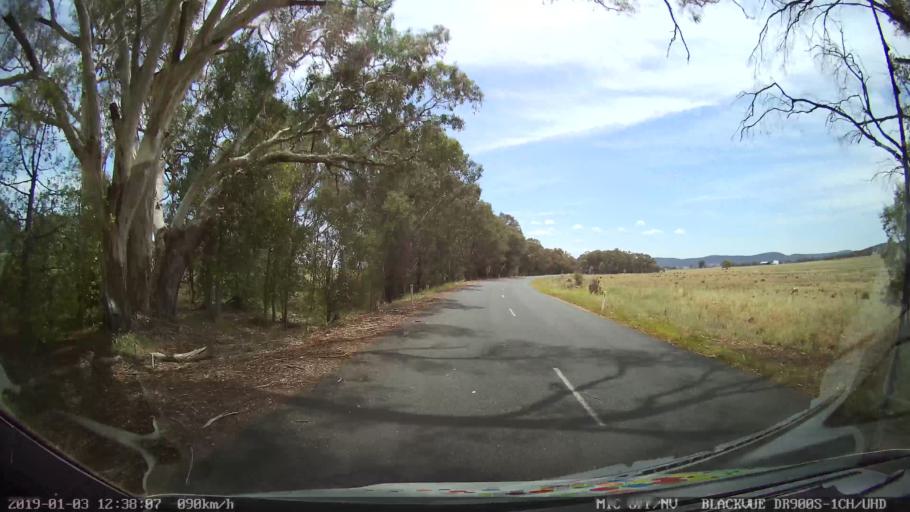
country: AU
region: New South Wales
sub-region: Weddin
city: Grenfell
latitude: -33.8361
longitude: 148.1918
